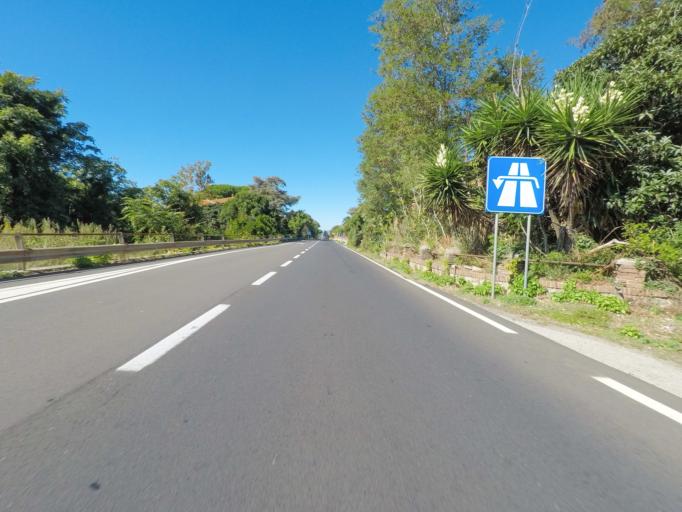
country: IT
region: Tuscany
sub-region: Provincia di Grosseto
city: Orbetello Scalo
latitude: 42.4515
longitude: 11.2542
